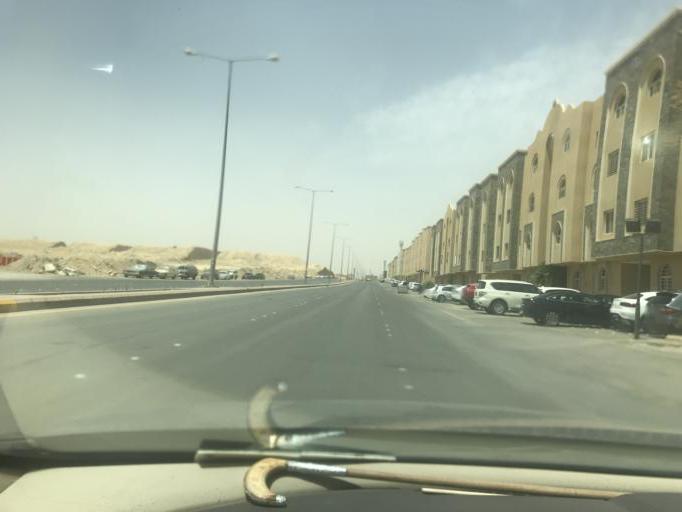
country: SA
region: Ar Riyad
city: Riyadh
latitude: 24.7912
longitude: 46.6699
